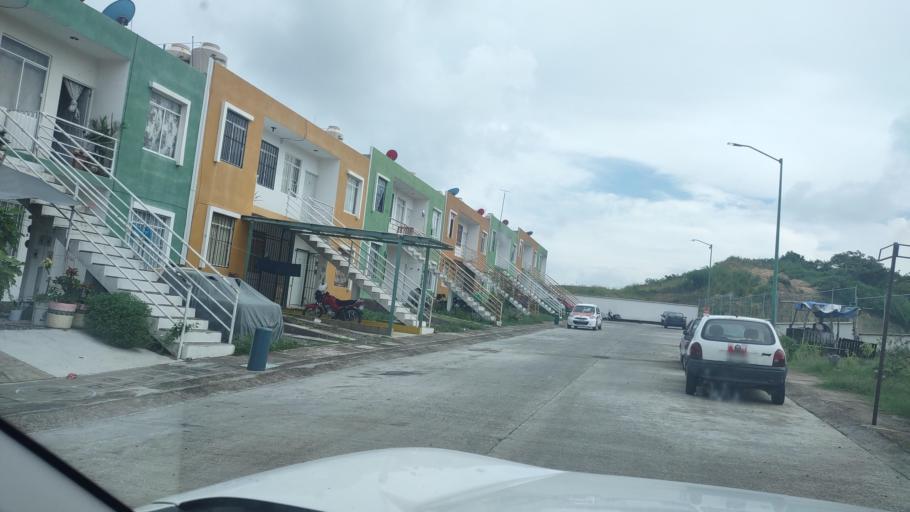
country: MX
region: Veracruz
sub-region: Tuxpan
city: Alto Lucero
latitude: 20.9571
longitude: -97.4382
